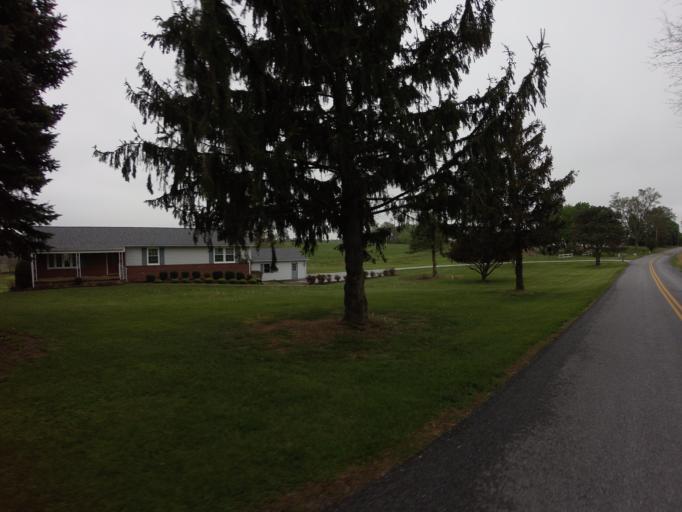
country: US
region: Maryland
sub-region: Baltimore County
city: Hunt Valley
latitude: 39.5751
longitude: -76.7202
